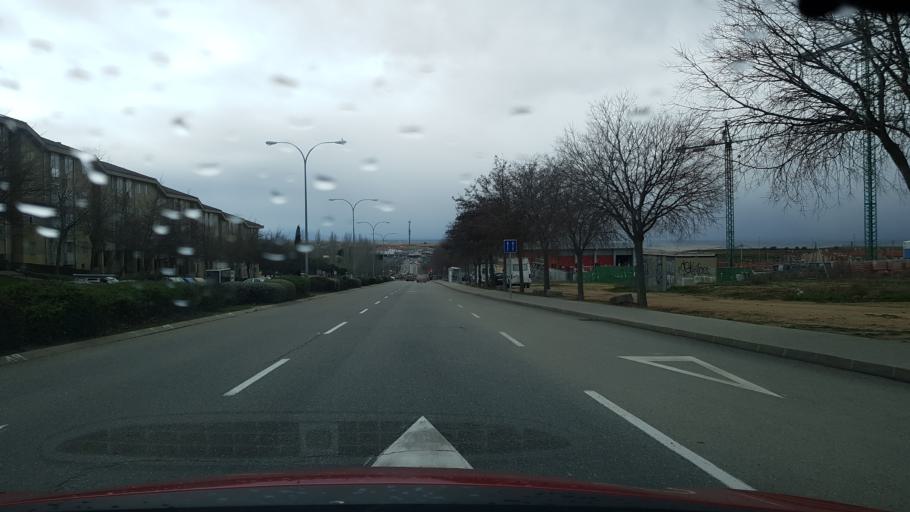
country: ES
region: Castille and Leon
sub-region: Provincia de Segovia
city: Segovia
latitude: 40.9347
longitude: -4.1017
